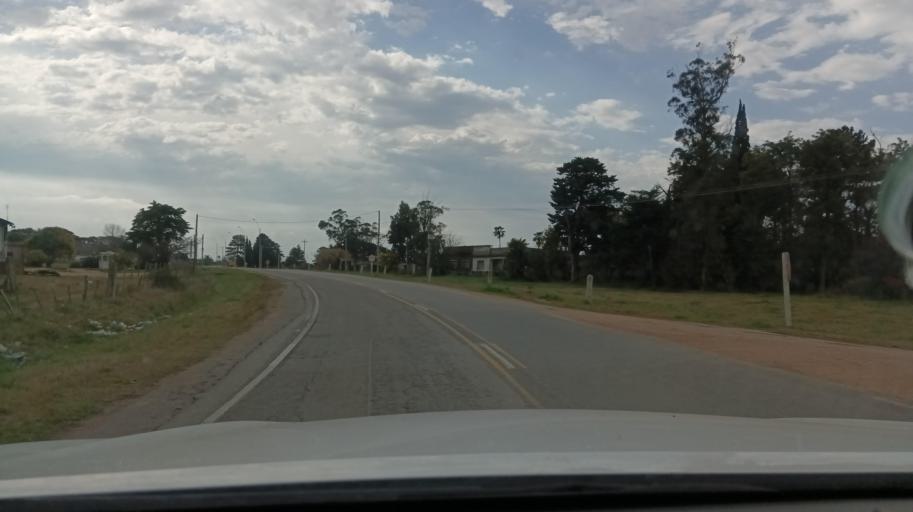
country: UY
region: Canelones
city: Toledo
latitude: -34.7065
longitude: -56.1051
